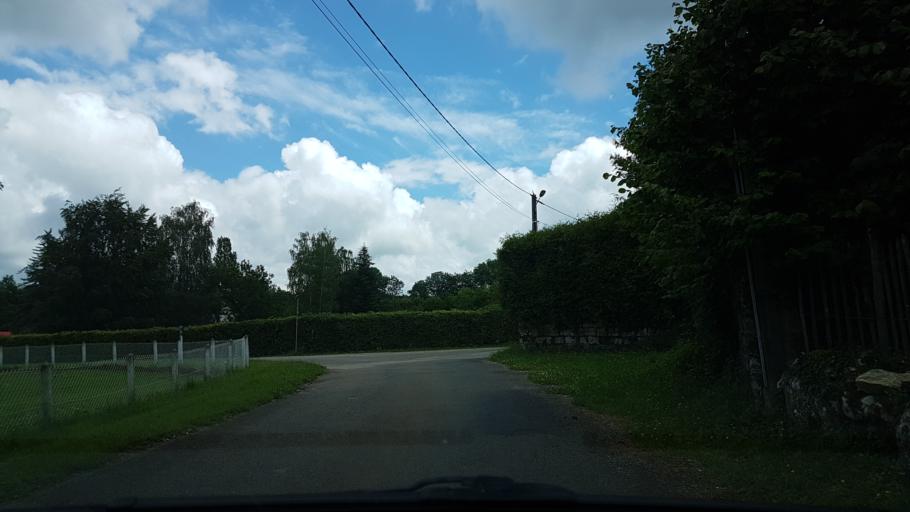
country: FR
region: Franche-Comte
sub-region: Departement du Jura
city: Clairvaux-les-Lacs
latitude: 46.5669
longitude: 5.7669
